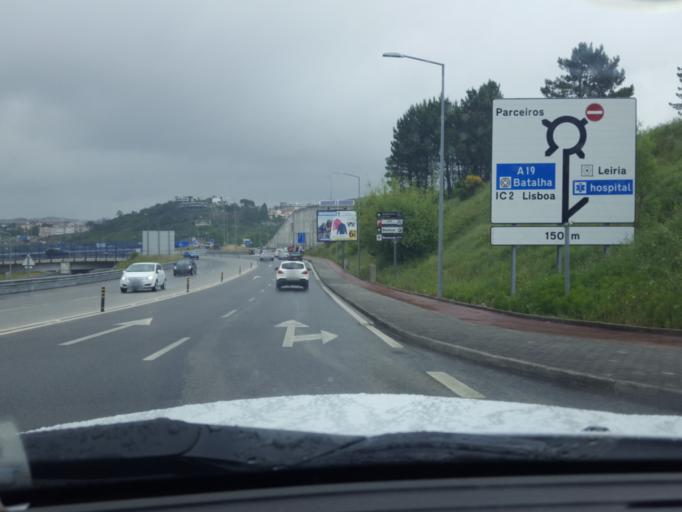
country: PT
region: Leiria
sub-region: Leiria
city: Leiria
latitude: 39.7352
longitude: -8.8232
